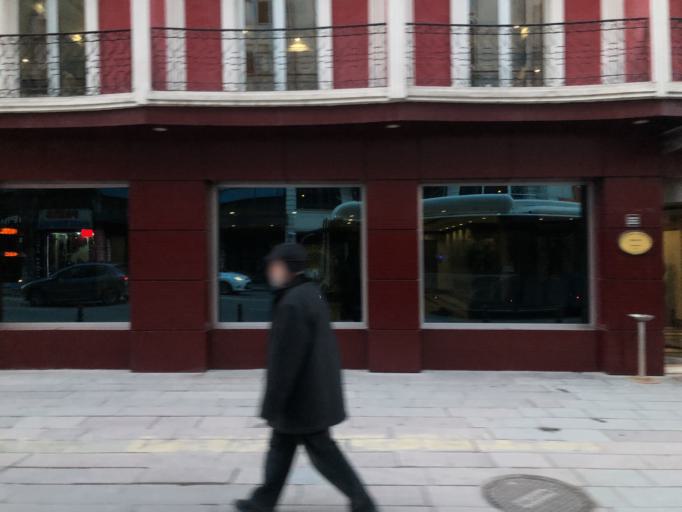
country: TR
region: Ankara
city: Ankara
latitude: 39.9453
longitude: 32.8546
